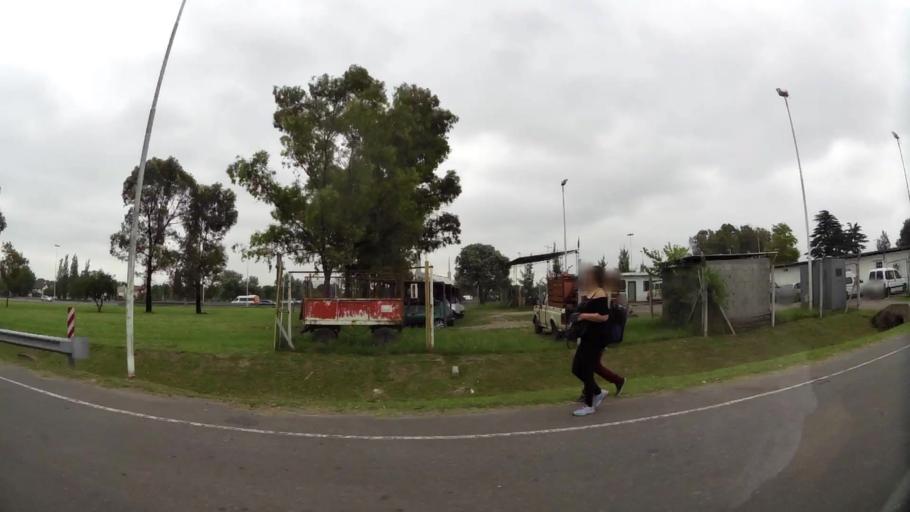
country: AR
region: Buenos Aires F.D.
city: Villa Lugano
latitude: -34.7301
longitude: -58.5157
